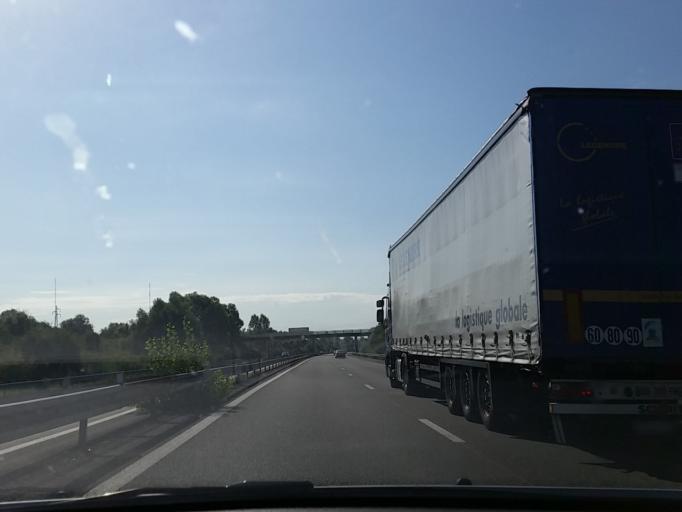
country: FR
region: Centre
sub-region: Departement du Cher
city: Foecy
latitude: 47.1879
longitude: 2.1662
